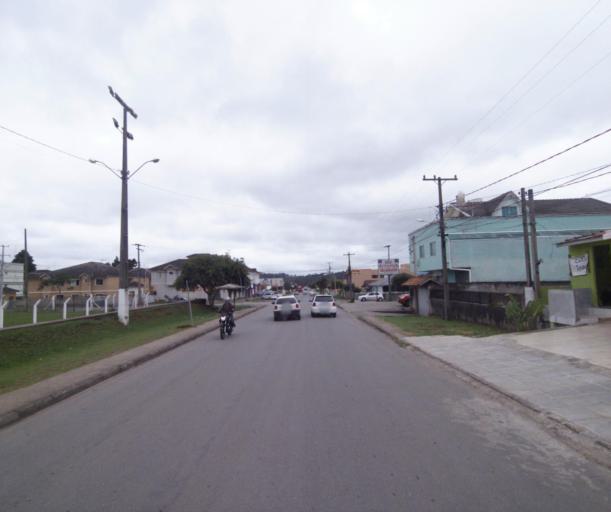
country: BR
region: Parana
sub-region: Quatro Barras
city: Quatro Barras
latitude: -25.3617
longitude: -49.1030
